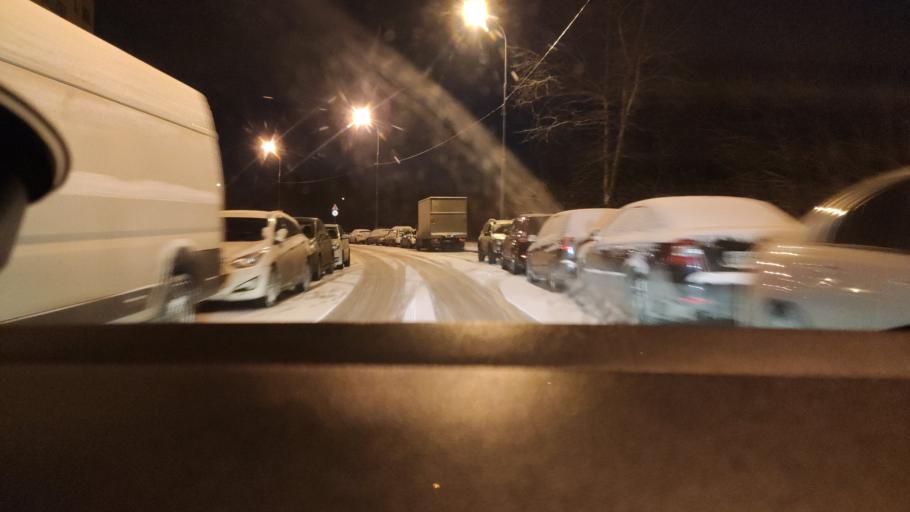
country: RU
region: Moscow
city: Annino
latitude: 55.5508
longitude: 37.5726
